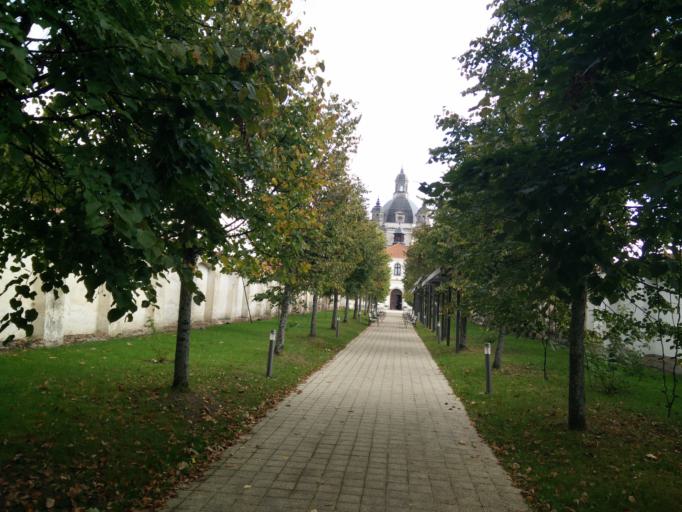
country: LT
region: Kauno apskritis
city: Dainava (Kaunas)
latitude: 54.8763
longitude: 24.0191
